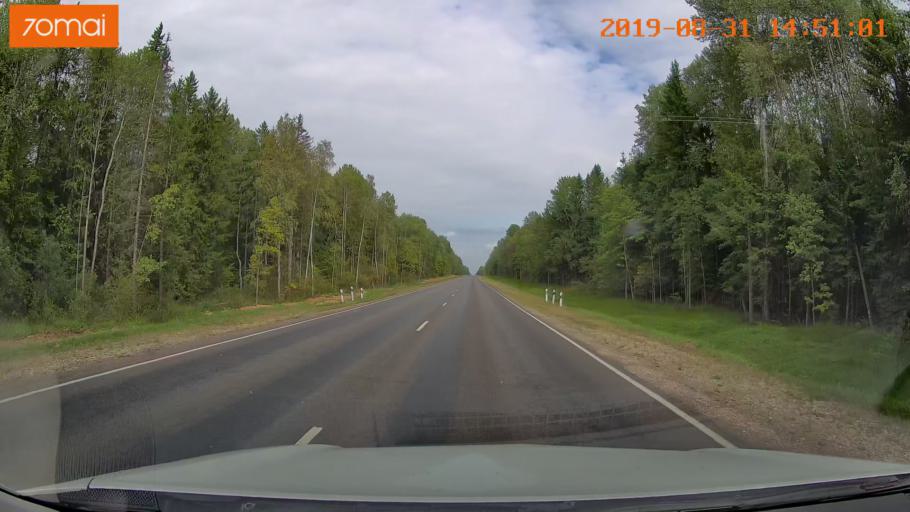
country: RU
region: Kaluga
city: Spas-Demensk
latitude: 54.2655
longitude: 33.8039
